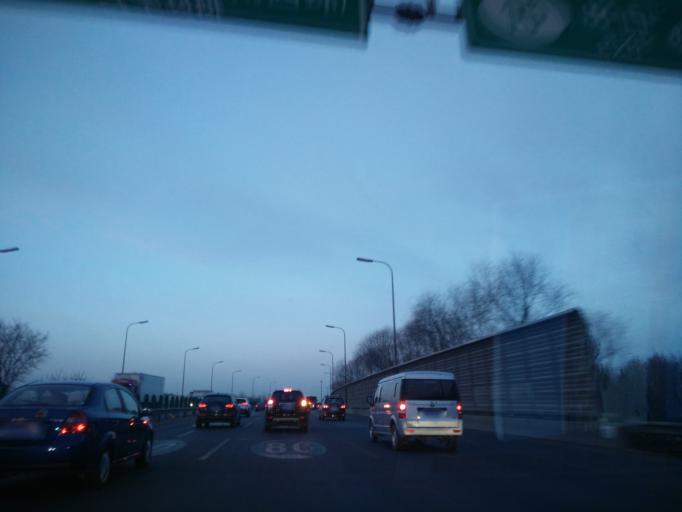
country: CN
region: Beijing
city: Jiugong
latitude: 39.8226
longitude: 116.5083
